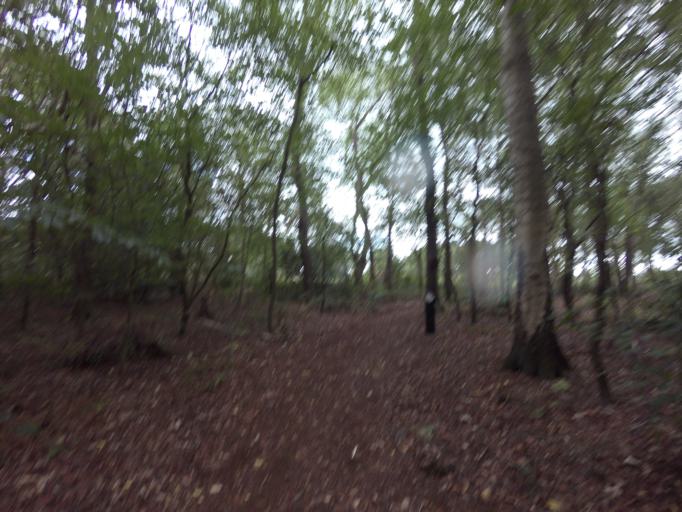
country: NL
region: Friesland
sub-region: Gemeente Heerenveen
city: Jubbega
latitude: 52.9583
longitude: 6.1829
